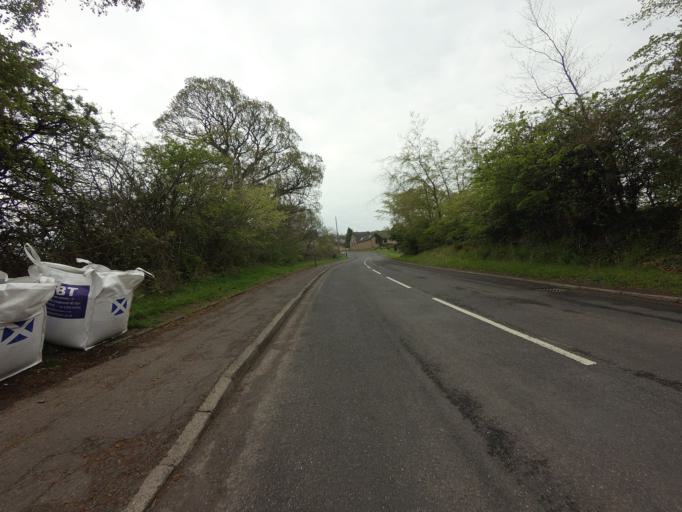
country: GB
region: Scotland
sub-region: Falkirk
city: Polmont
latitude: 55.9790
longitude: -3.7372
